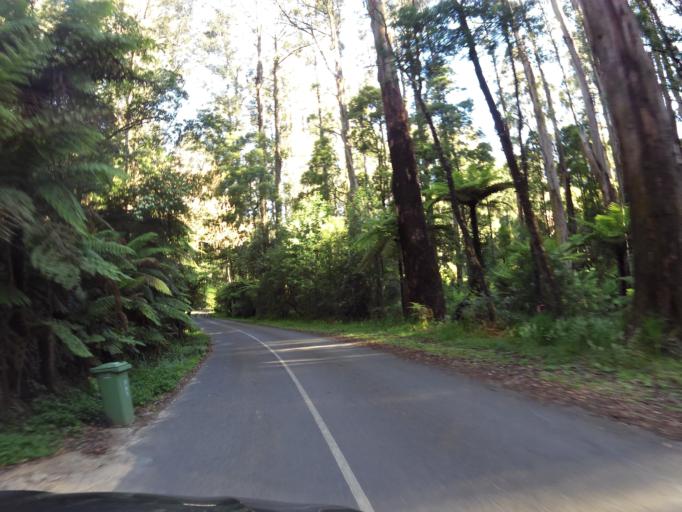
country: AU
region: Victoria
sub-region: Yarra Ranges
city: Kallista
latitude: -37.8688
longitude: 145.3601
